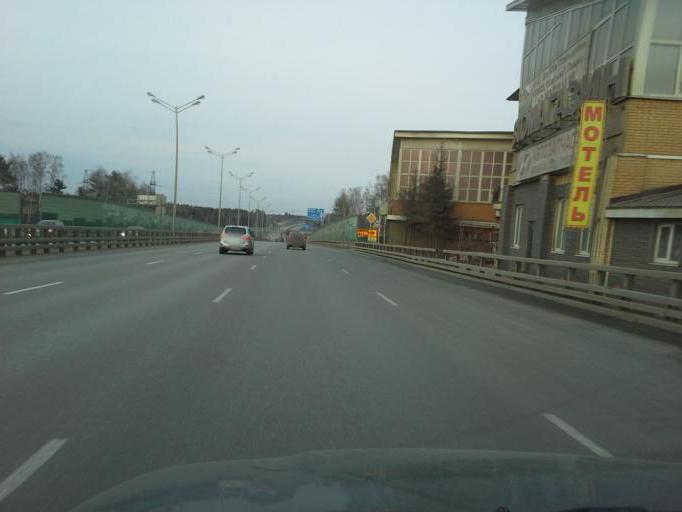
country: RU
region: Moskovskaya
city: Lesnoy Gorodok
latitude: 55.6369
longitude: 37.2233
